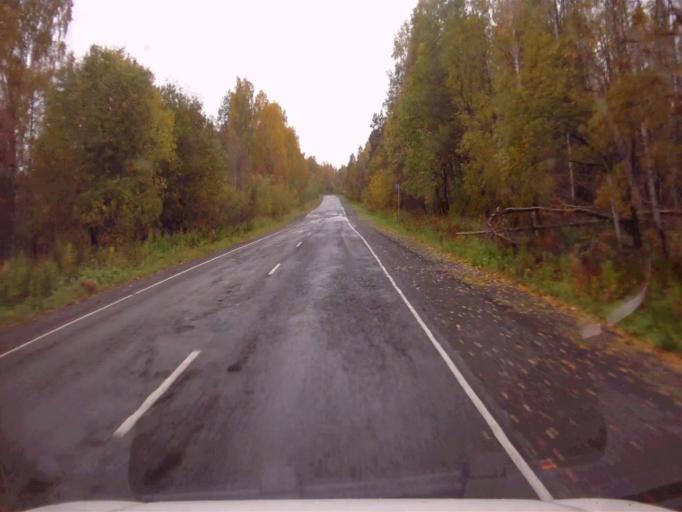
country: RU
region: Chelyabinsk
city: Nizhniy Ufaley
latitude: 56.0548
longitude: 60.0468
